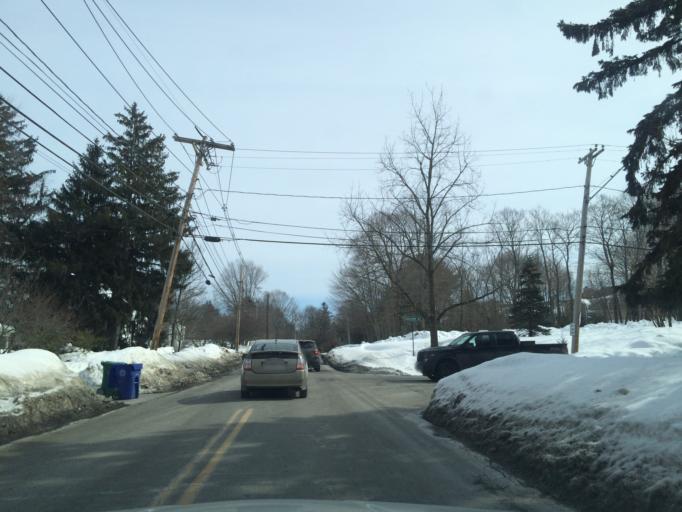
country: US
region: Massachusetts
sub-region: Middlesex County
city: Newton
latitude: 42.3089
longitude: -71.1997
